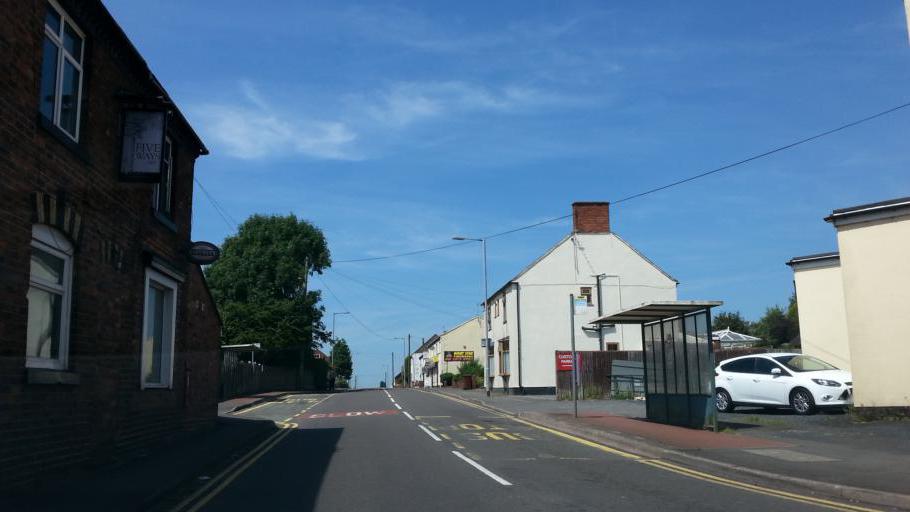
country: GB
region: England
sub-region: Staffordshire
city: Norton Canes
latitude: 52.6872
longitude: -1.9779
